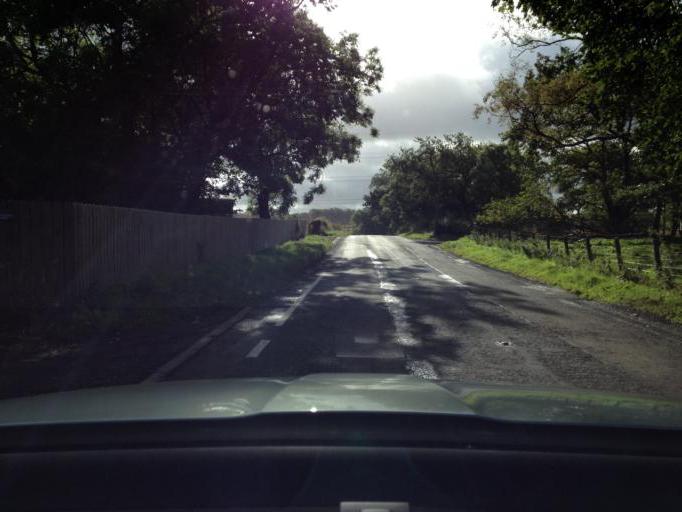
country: GB
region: Scotland
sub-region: West Lothian
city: West Calder
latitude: 55.8433
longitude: -3.5427
